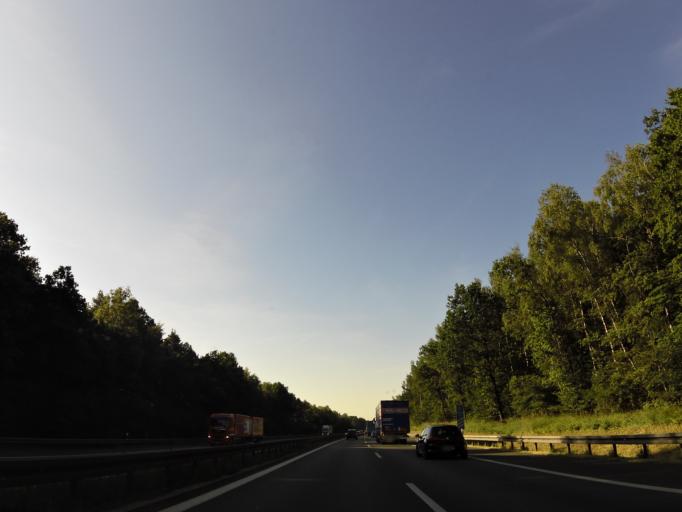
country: DE
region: Bavaria
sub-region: Regierungsbezirk Mittelfranken
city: Hessdorf
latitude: 49.6351
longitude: 10.9158
